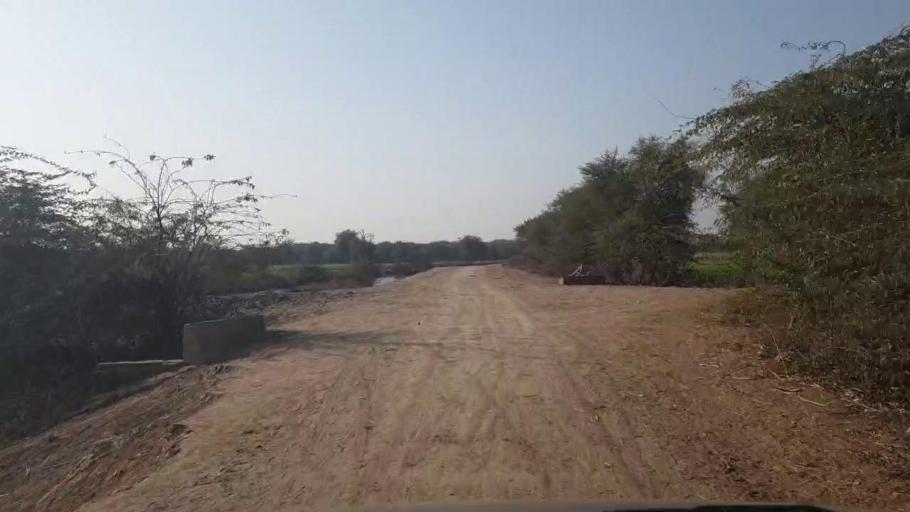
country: PK
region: Sindh
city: Tando Adam
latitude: 25.7248
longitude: 68.6064
